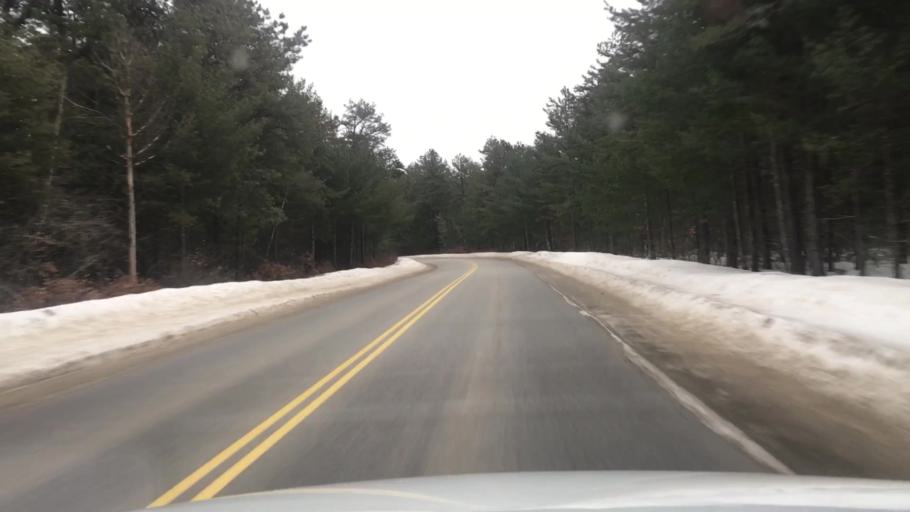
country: US
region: Maine
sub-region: York County
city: Newfield
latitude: 43.6012
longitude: -70.8754
